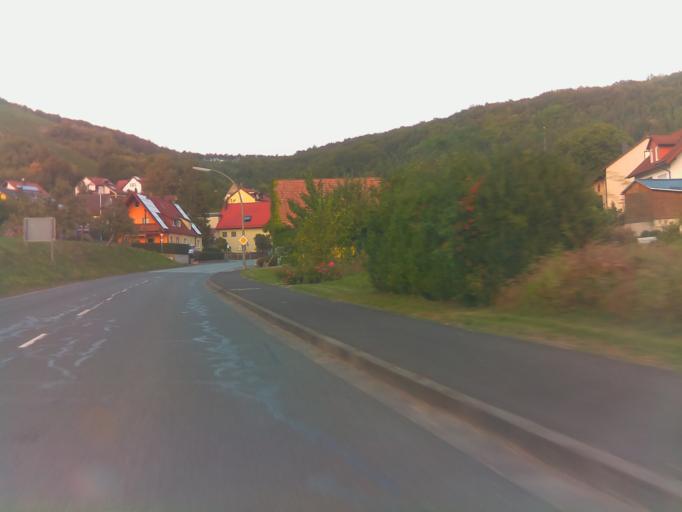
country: DE
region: Bavaria
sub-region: Regierungsbezirk Unterfranken
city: Ramsthal
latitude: 50.1387
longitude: 10.0648
